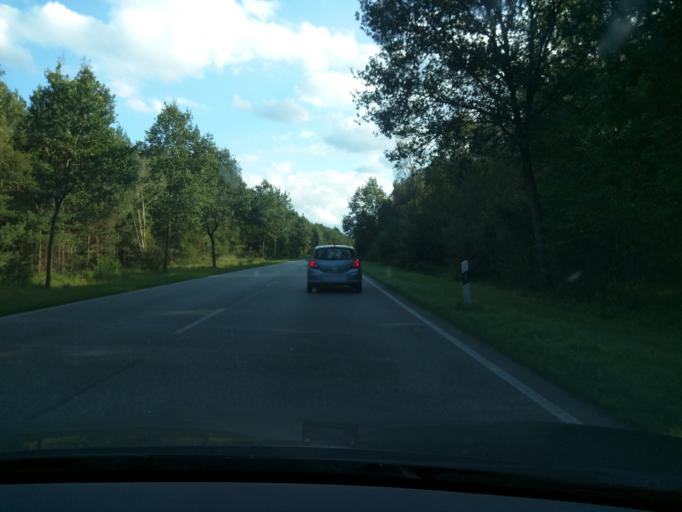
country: DE
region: Schleswig-Holstein
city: Escheburg
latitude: 53.4451
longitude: 10.3368
